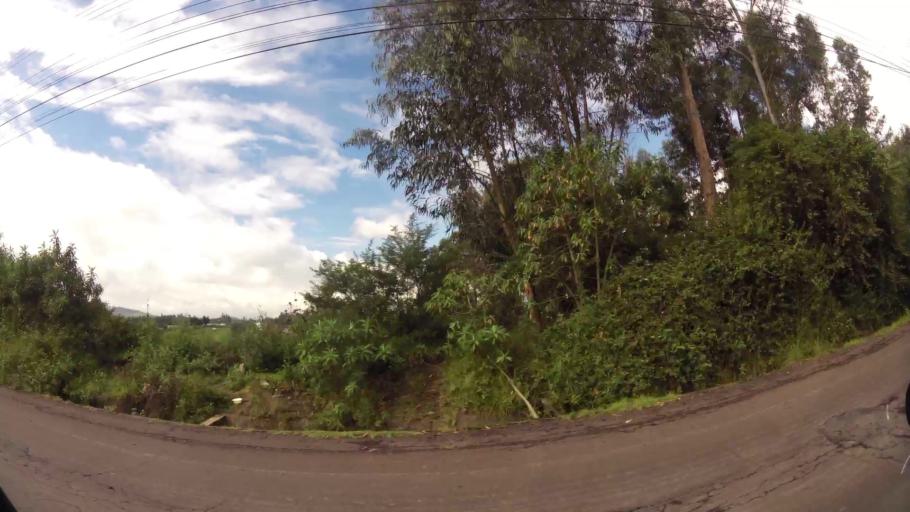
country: EC
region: Pichincha
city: Sangolqui
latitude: -0.3126
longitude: -78.4082
